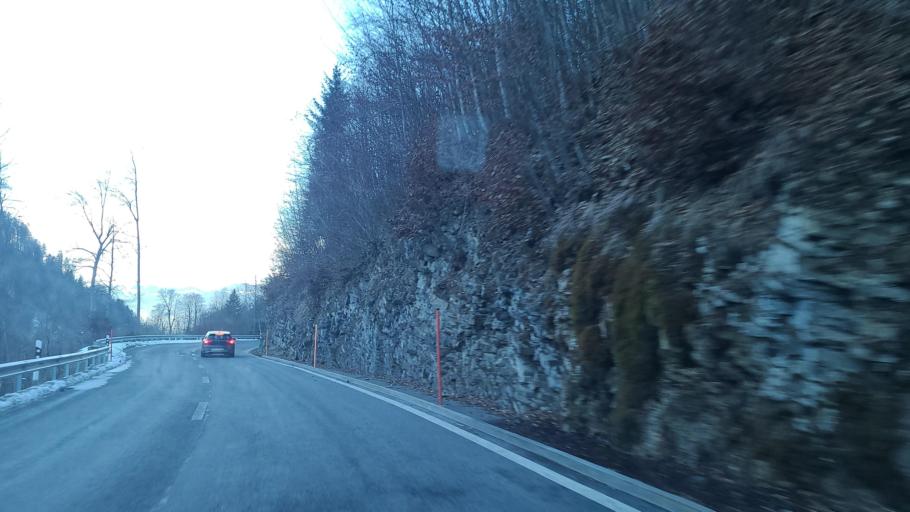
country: CH
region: Obwalden
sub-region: Obwalden
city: Kerns
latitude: 46.8557
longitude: 8.2926
